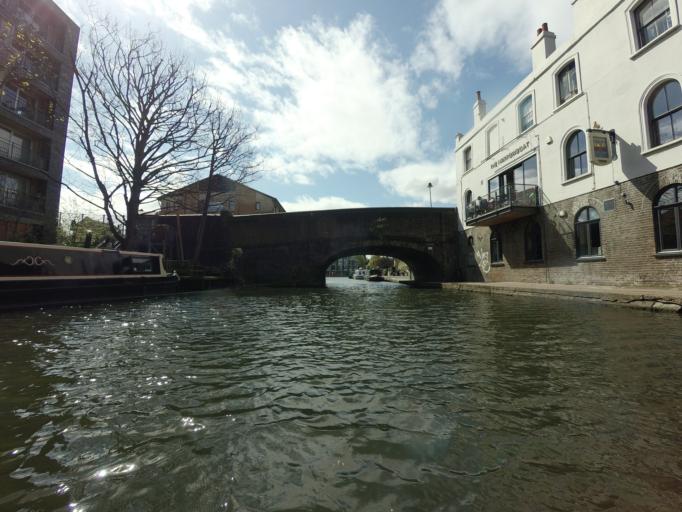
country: GB
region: England
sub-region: Greater London
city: Islington
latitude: 51.5330
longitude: -0.0966
